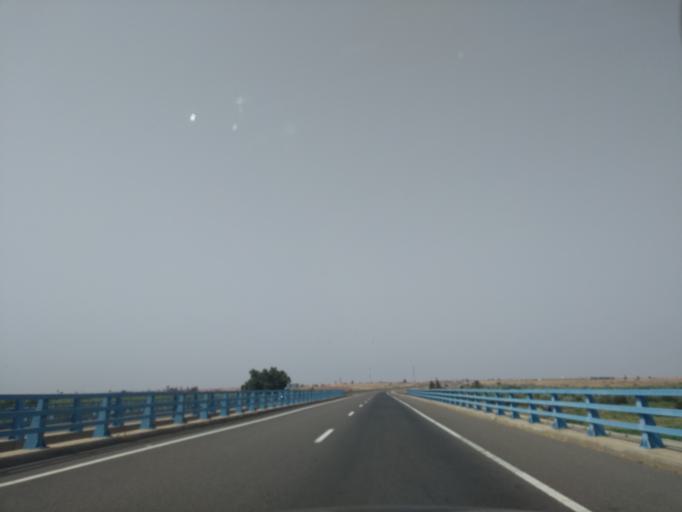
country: MA
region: Marrakech-Tensift-Al Haouz
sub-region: Marrakech
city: Marrakesh
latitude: 31.7315
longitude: -8.2186
